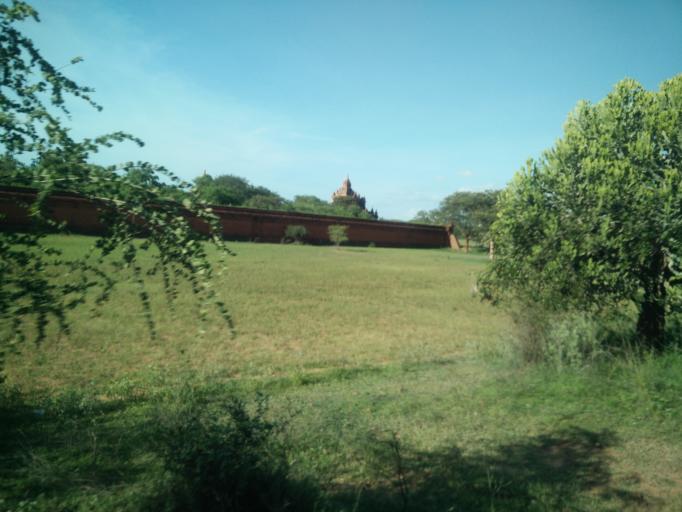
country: MM
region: Magway
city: Pakokku
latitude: 21.1637
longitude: 94.8815
